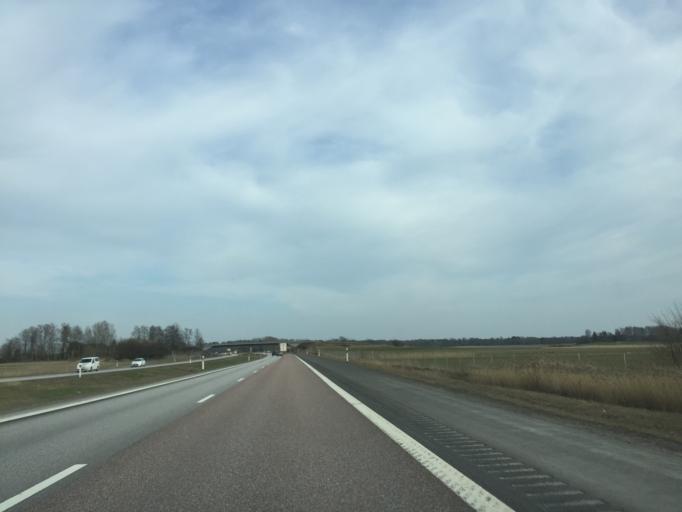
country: SE
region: OErebro
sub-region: Orebro Kommun
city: Hovsta
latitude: 59.3067
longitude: 15.3627
